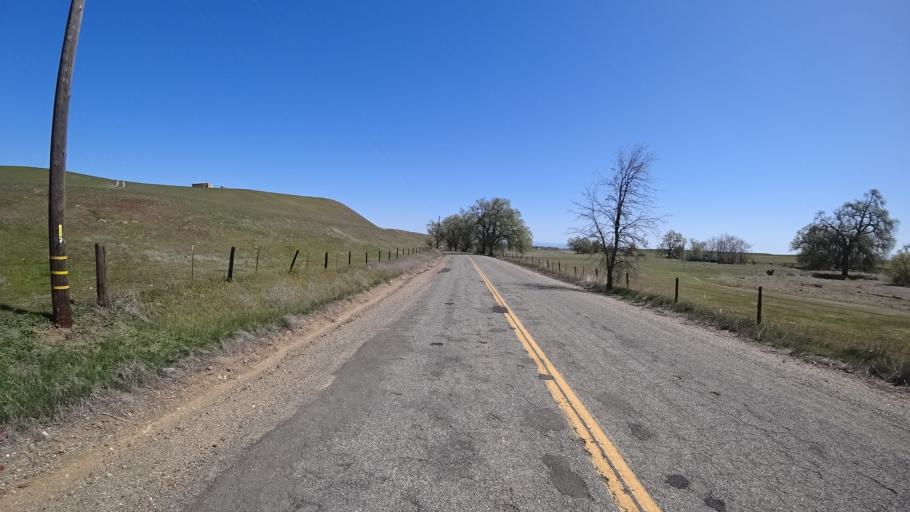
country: US
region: California
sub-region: Glenn County
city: Orland
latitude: 39.7784
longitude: -122.3115
